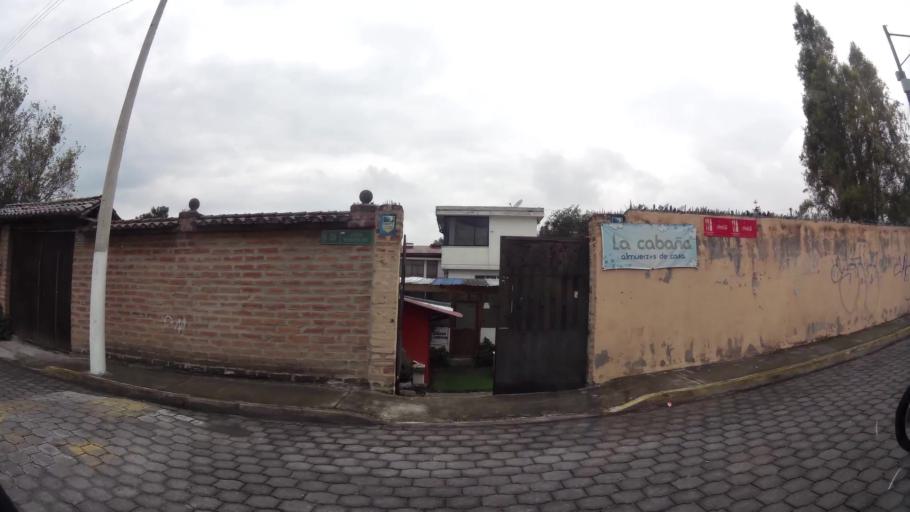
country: EC
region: Pichincha
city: Sangolqui
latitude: -0.3045
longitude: -78.4741
